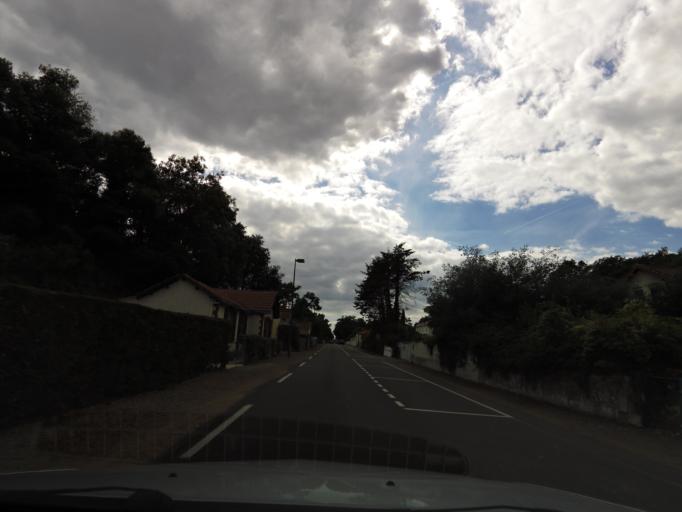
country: FR
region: Pays de la Loire
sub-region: Departement de la Vendee
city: Longeville-sur-Mer
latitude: 46.4067
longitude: -1.4983
